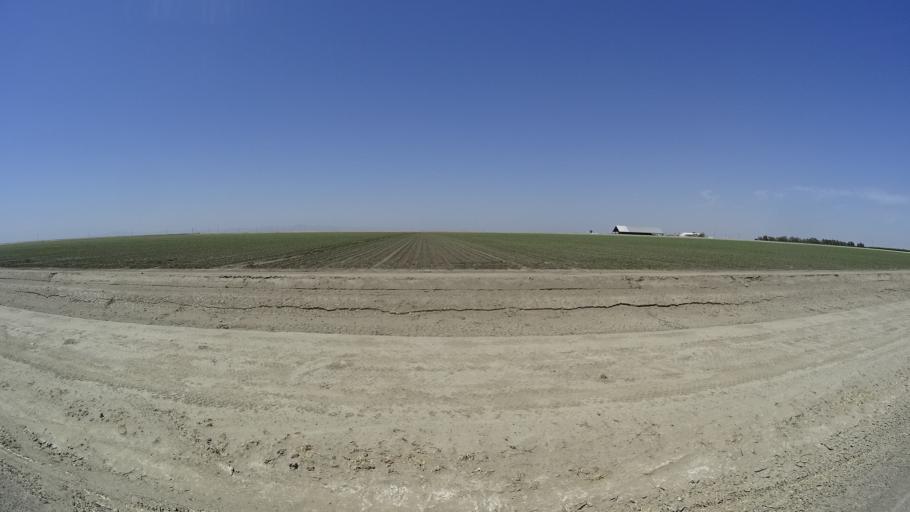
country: US
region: California
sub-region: Kings County
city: Corcoran
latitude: 36.1022
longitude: -119.6257
